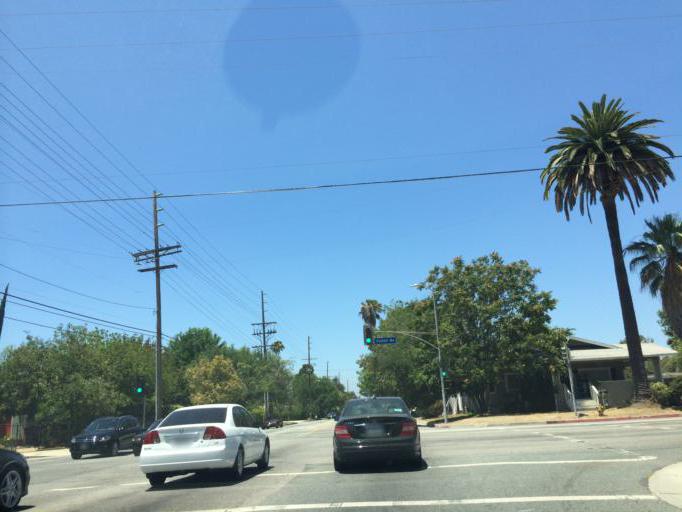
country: US
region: California
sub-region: Los Angeles County
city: Sherman Oaks
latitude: 34.1649
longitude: -118.4223
